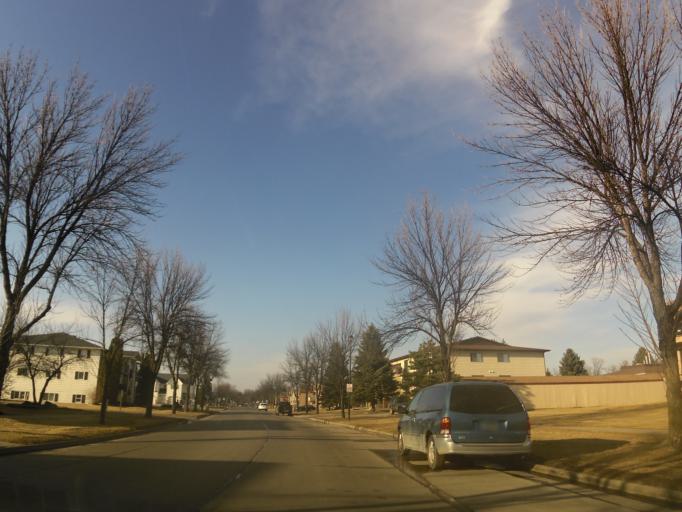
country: US
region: North Dakota
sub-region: Grand Forks County
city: Grand Forks
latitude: 47.8921
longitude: -97.0512
